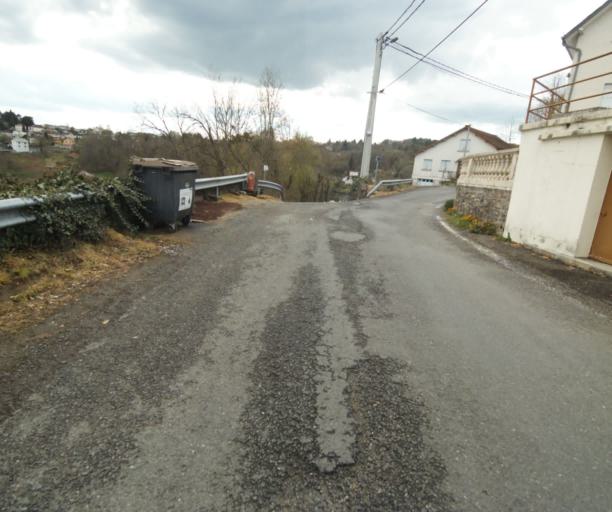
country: FR
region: Limousin
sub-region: Departement de la Correze
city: Tulle
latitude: 45.2629
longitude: 1.7508
